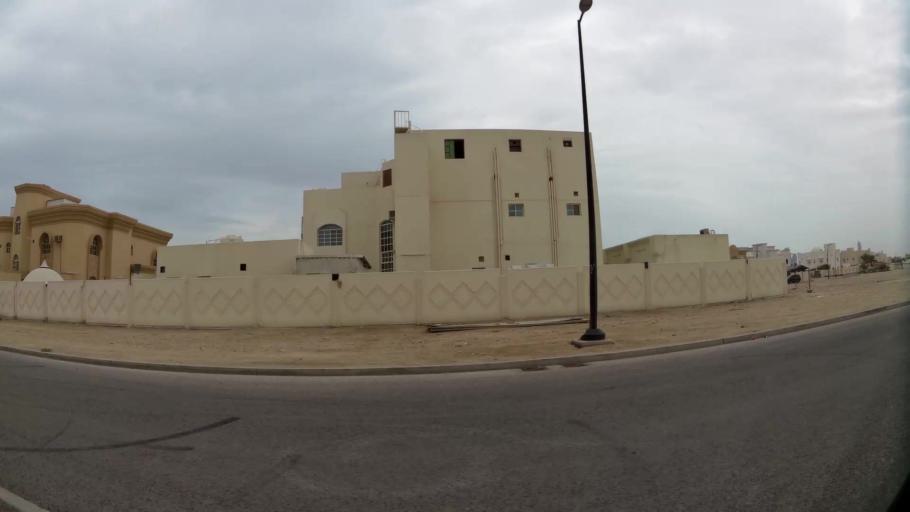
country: QA
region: Baladiyat ad Dawhah
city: Doha
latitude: 25.3470
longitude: 51.4999
